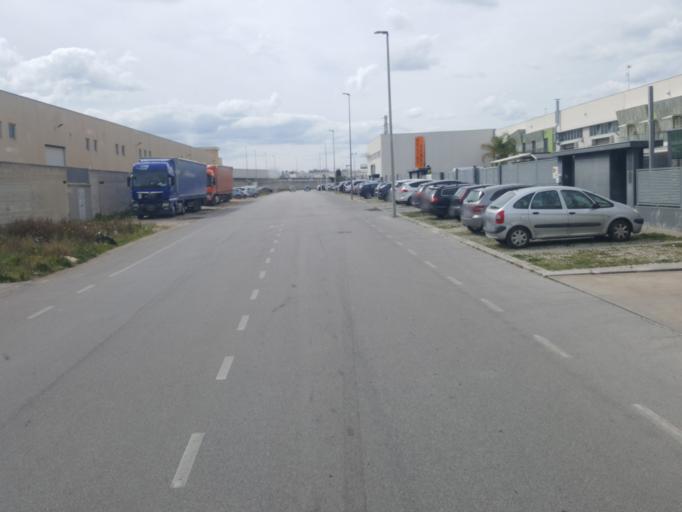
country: IT
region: Apulia
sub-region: Provincia di Bari
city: Modugno
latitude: 41.0944
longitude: 16.7958
